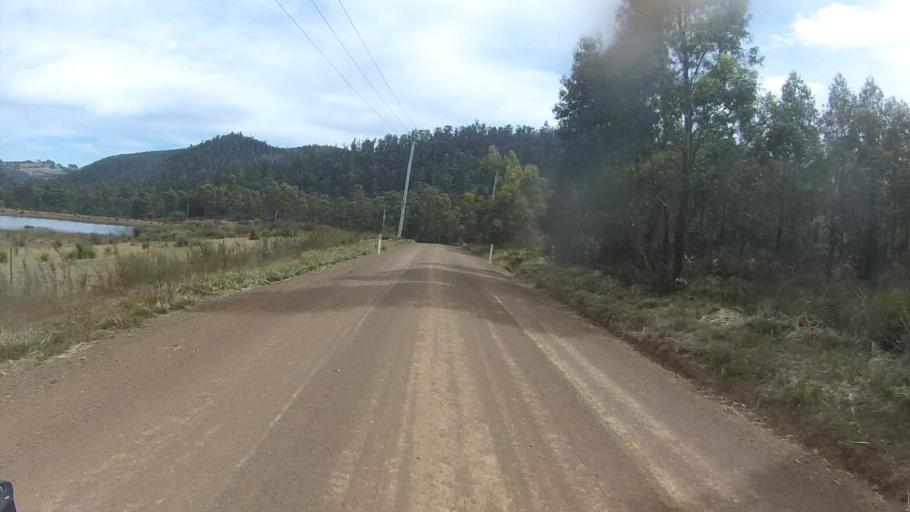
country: AU
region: Tasmania
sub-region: Sorell
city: Sorell
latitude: -42.7555
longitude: 147.7999
